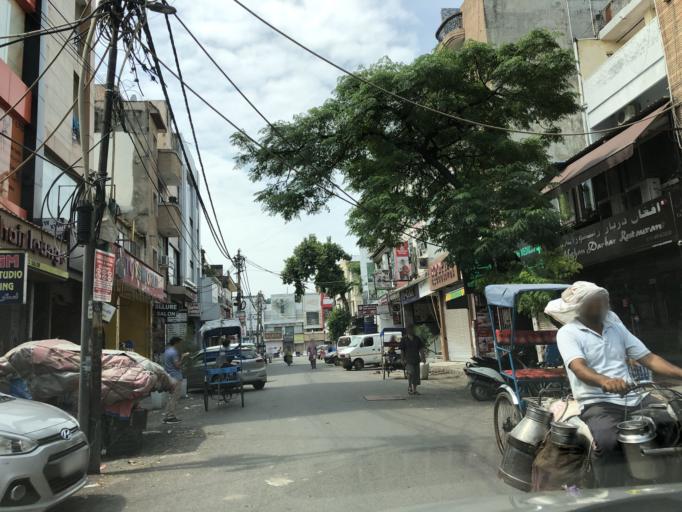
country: IN
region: NCT
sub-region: New Delhi
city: New Delhi
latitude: 28.5707
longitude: 77.2425
